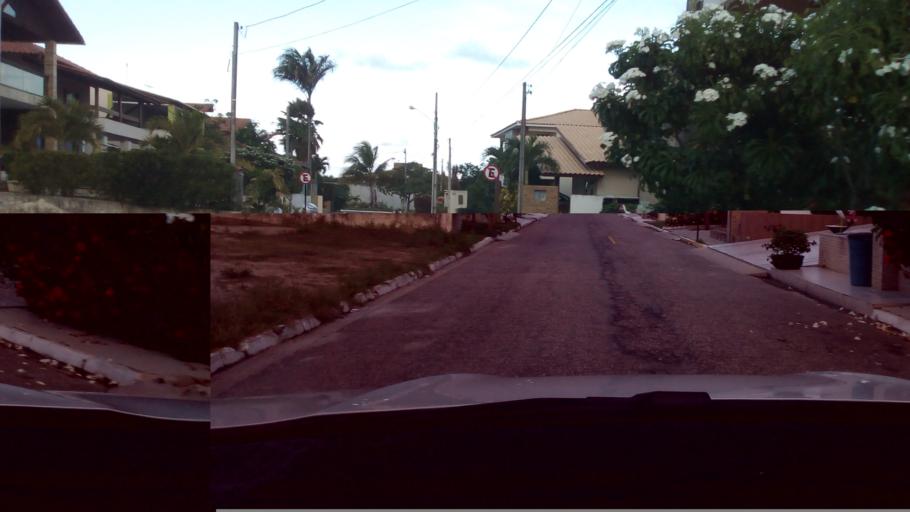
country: BR
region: Paraiba
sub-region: Joao Pessoa
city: Joao Pessoa
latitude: -7.1602
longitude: -34.8053
